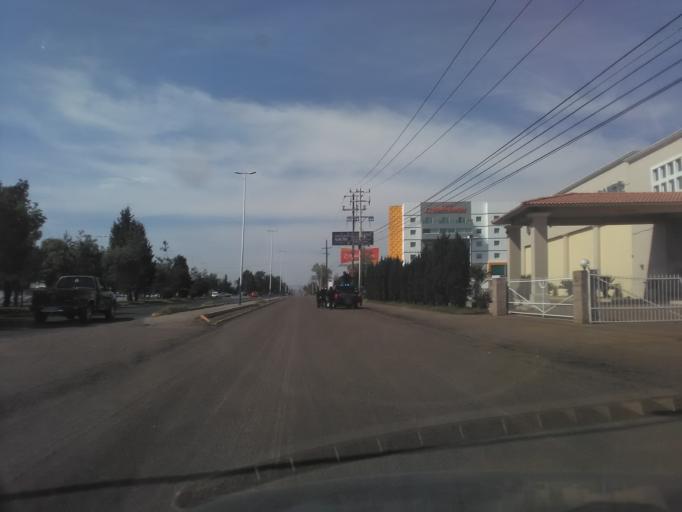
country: MX
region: Durango
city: Victoria de Durango
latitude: 24.0557
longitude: -104.6143
